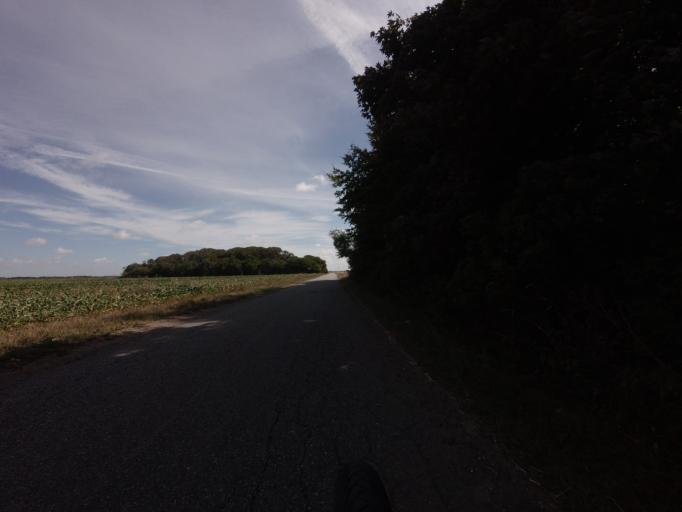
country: DK
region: North Denmark
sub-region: Jammerbugt Kommune
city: Pandrup
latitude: 57.3428
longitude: 9.7849
